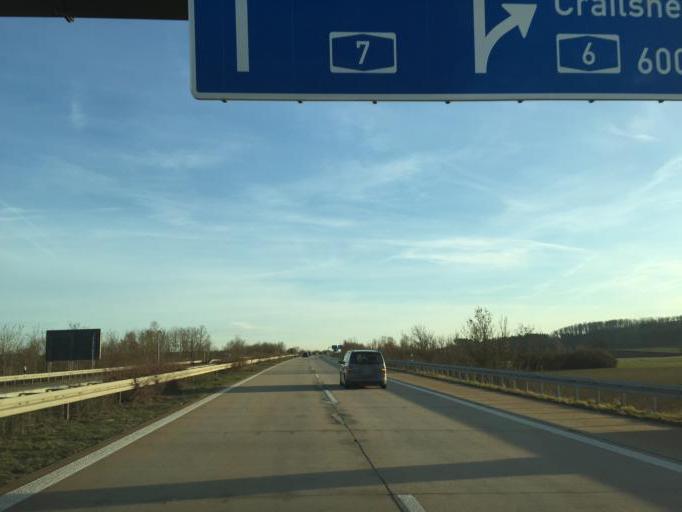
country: DE
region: Bavaria
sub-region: Regierungsbezirk Mittelfranken
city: Schnelldorf
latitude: 49.2151
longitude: 10.2250
